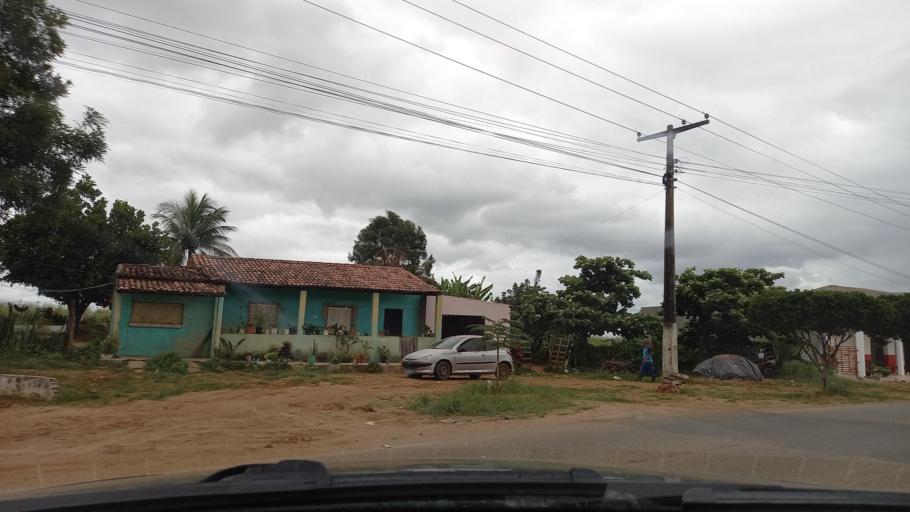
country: BR
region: Sergipe
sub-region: Caninde De Sao Francisco
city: Caninde de Sao Francisco
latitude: -9.6789
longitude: -37.7911
